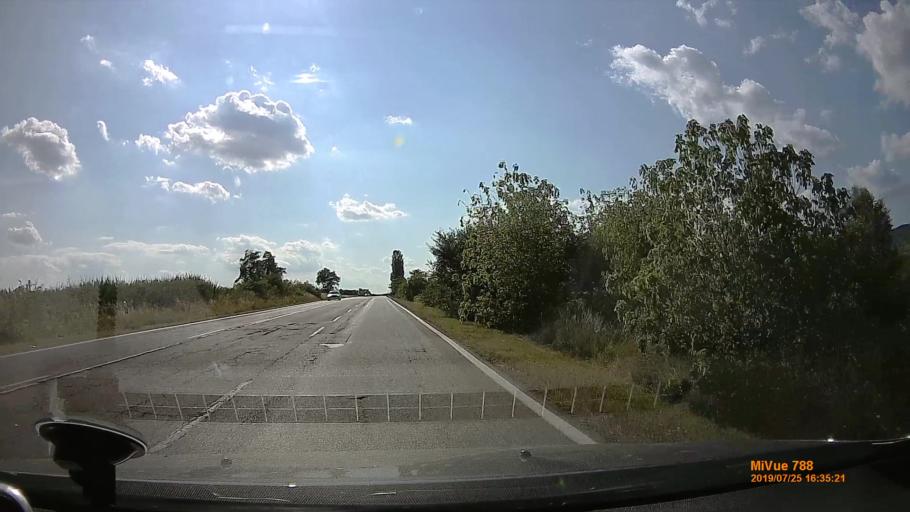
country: HU
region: Heves
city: Abasar
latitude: 47.7671
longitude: 20.0053
